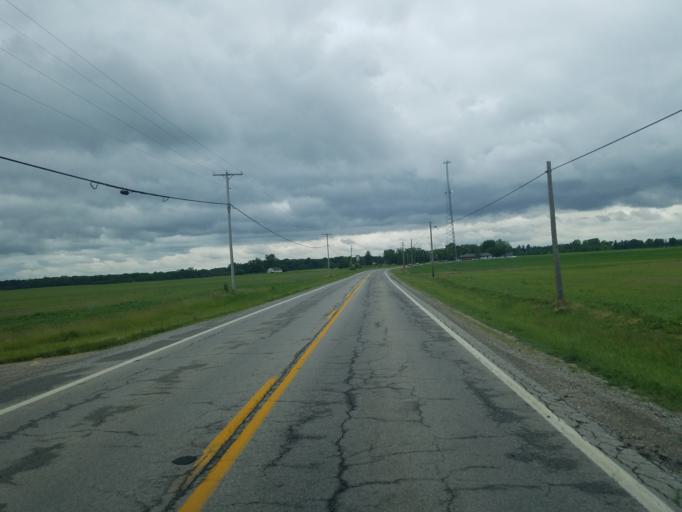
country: US
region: Ohio
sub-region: Marion County
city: Marion
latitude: 40.6297
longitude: -83.1395
